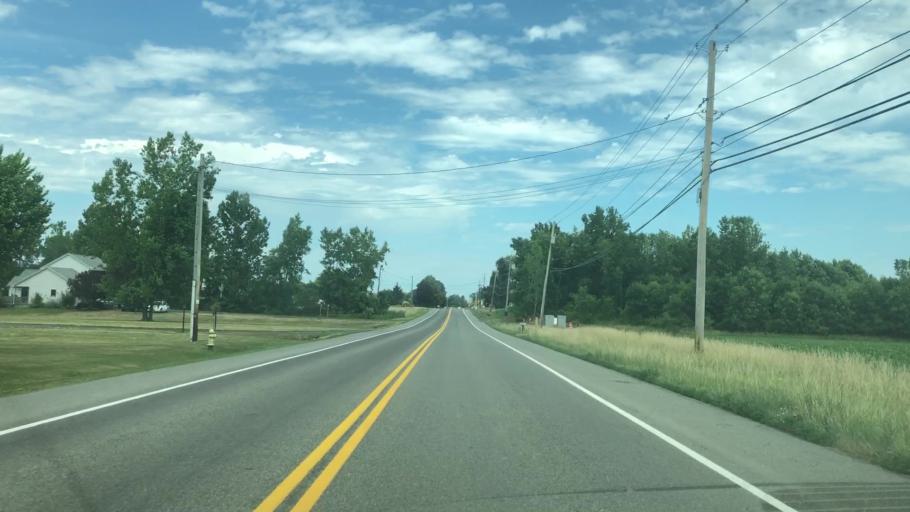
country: US
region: New York
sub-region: Monroe County
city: Webster
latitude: 43.2008
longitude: -77.4005
